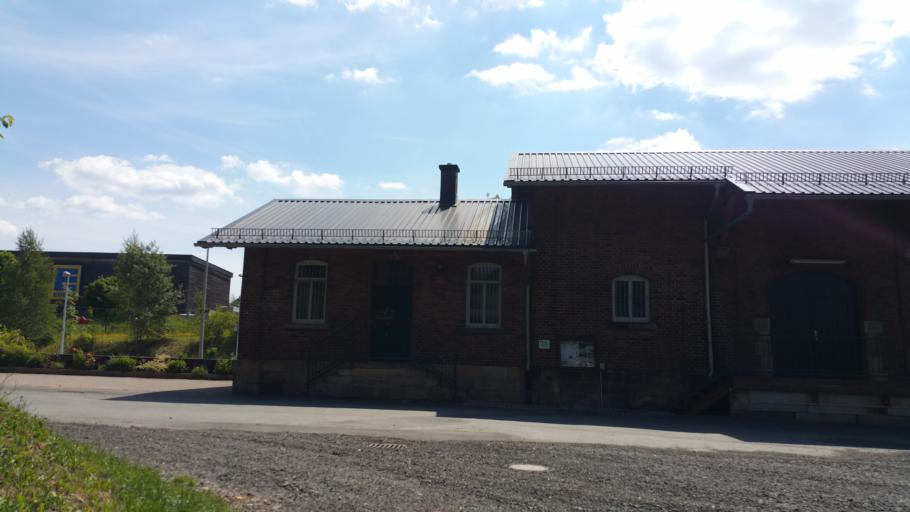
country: DE
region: Bavaria
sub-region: Upper Franconia
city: Schwarzenbach an der Saale
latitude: 50.2200
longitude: 11.9349
